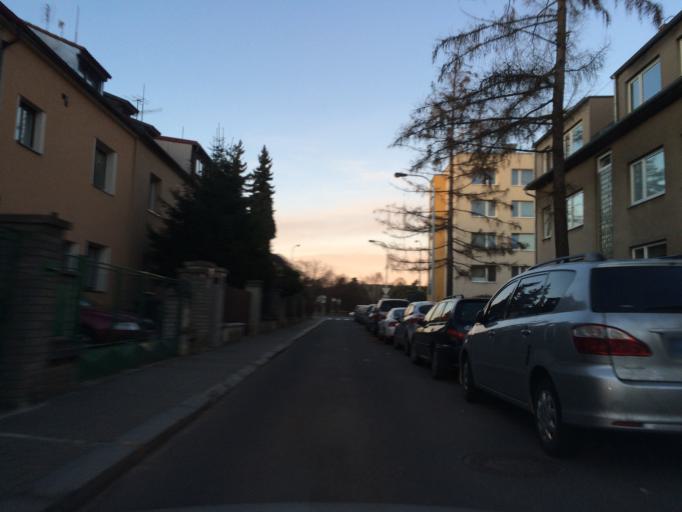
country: CZ
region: Central Bohemia
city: Horomerice
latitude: 50.0916
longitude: 14.3213
